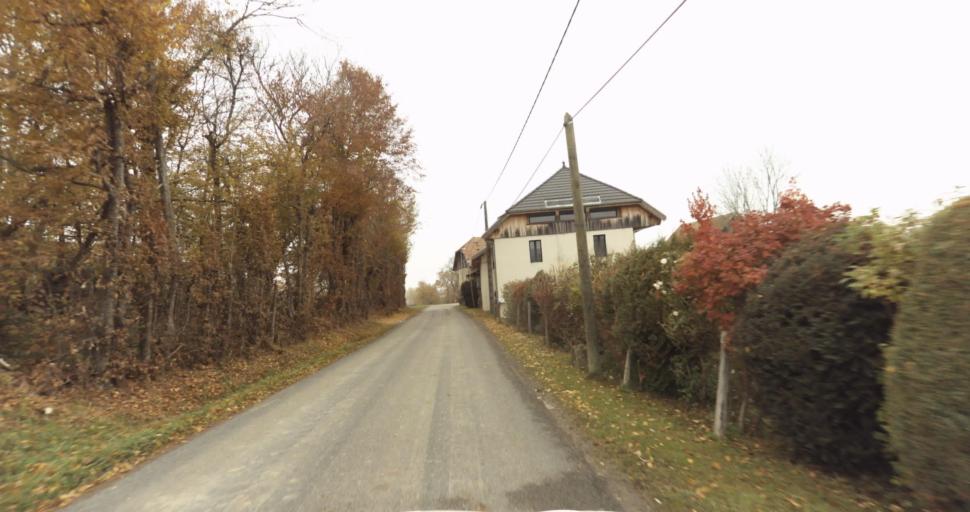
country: FR
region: Rhone-Alpes
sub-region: Departement de la Haute-Savoie
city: Cusy
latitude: 45.7826
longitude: 6.0113
